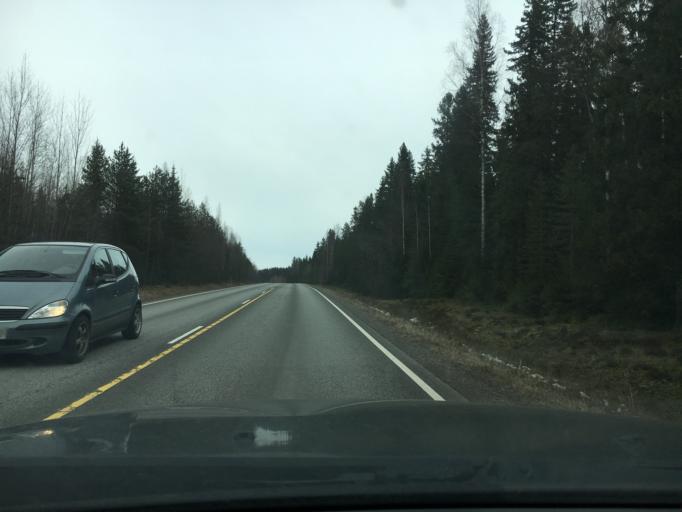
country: FI
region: Central Finland
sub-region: AEaenekoski
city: Konnevesi
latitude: 62.5965
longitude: 26.2035
